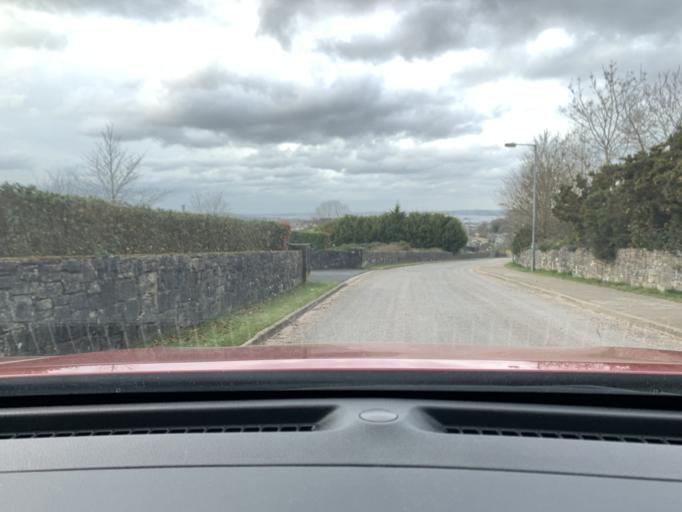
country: IE
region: Connaught
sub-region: Sligo
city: Sligo
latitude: 54.2563
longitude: -8.4547
